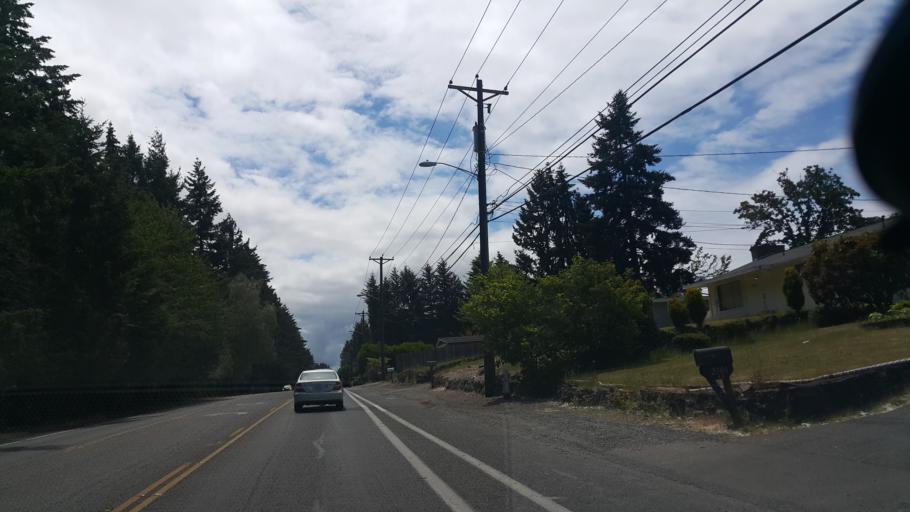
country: US
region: Washington
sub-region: Pierce County
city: Fircrest
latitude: 47.2352
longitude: -122.5264
